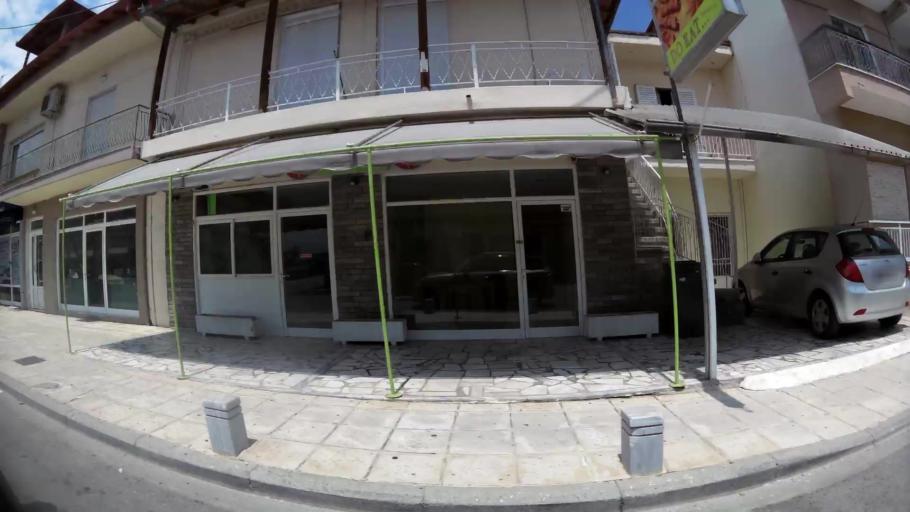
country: GR
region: Central Macedonia
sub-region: Nomos Pierias
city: Peristasi
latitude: 40.2701
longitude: 22.5276
